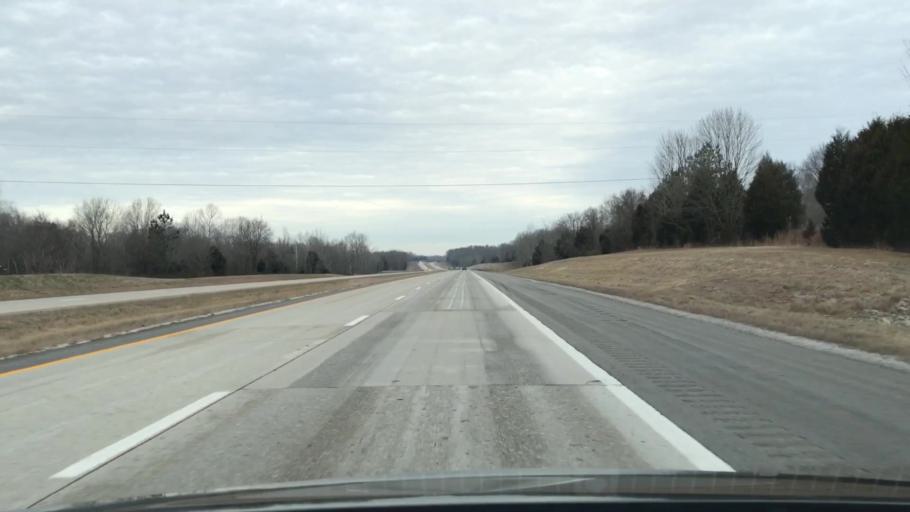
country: US
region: Kentucky
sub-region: Ohio County
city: Oak Grove
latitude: 37.3401
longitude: -86.7665
